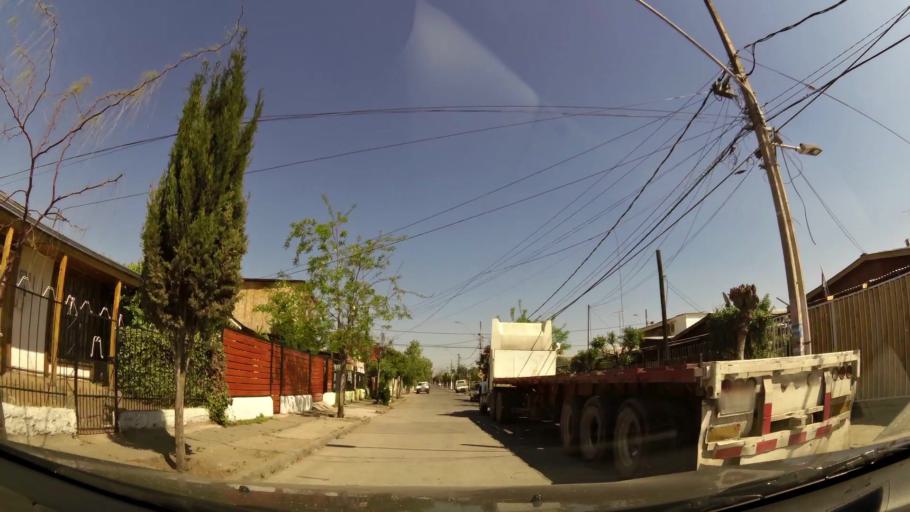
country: CL
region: Santiago Metropolitan
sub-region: Provincia de Maipo
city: San Bernardo
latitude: -33.5781
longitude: -70.7015
